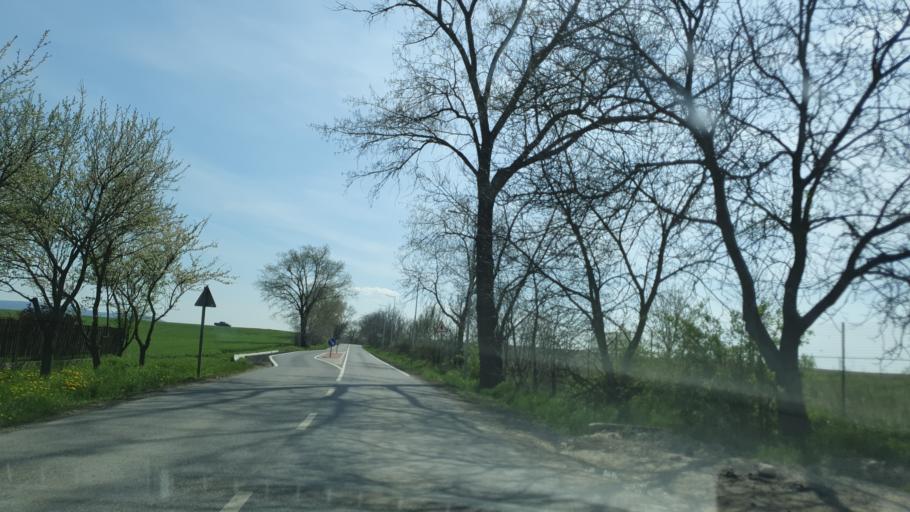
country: HU
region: Komarom-Esztergom
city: Bokod
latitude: 47.4898
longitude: 18.2425
